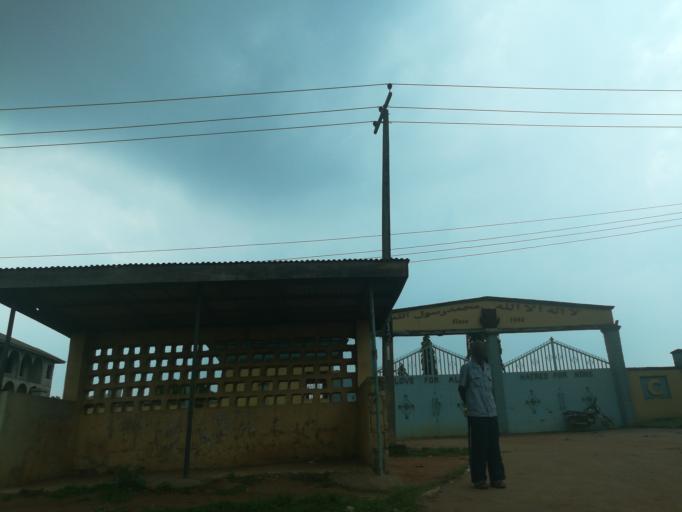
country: NG
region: Lagos
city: Ikorodu
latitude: 6.5837
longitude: 3.5877
